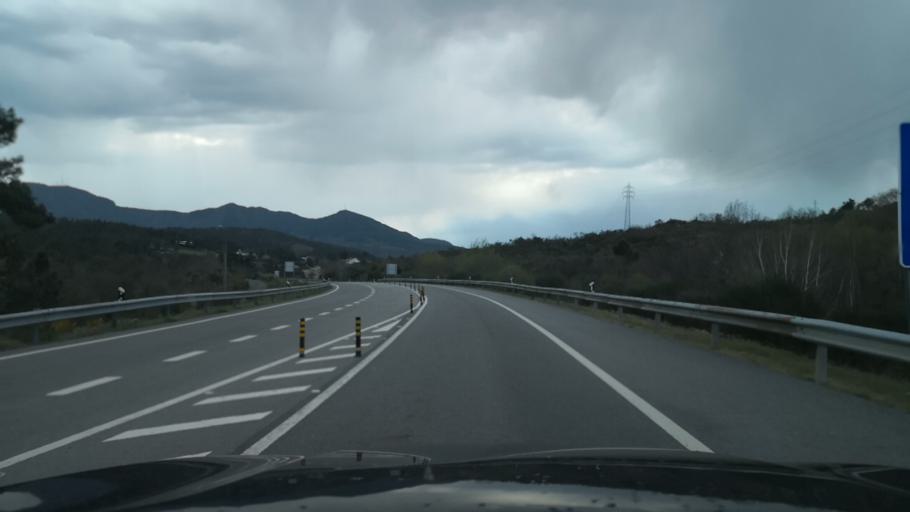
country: PT
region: Vila Real
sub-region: Santa Marta de Penaguiao
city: Santa Marta de Penaguiao
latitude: 41.2848
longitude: -7.8190
